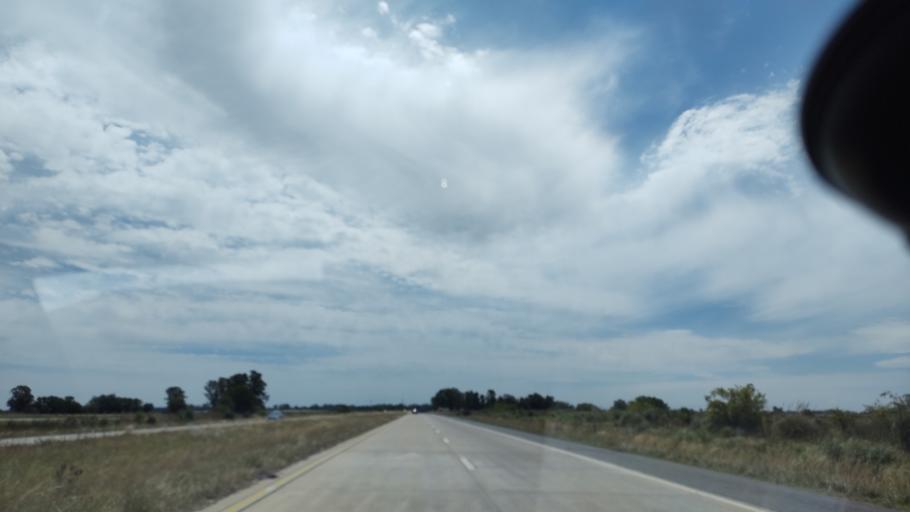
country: AR
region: Buenos Aires
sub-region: Partido de Brandsen
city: Brandsen
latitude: -35.0330
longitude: -58.1974
